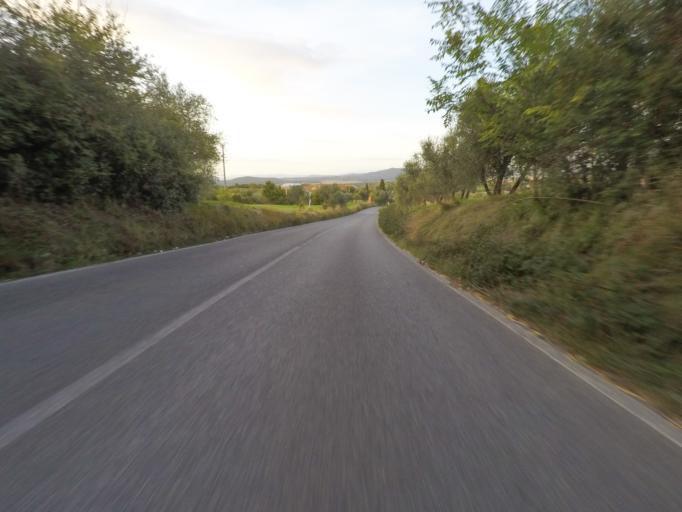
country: IT
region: Tuscany
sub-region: Provincia di Siena
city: Pienza
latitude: 43.0808
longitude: 11.6764
